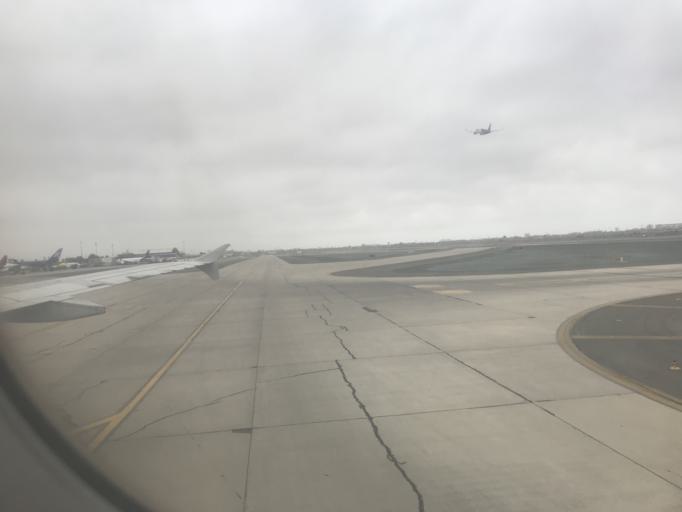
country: PE
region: Callao
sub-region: Callao
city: Callao
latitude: -12.0238
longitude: -77.1112
